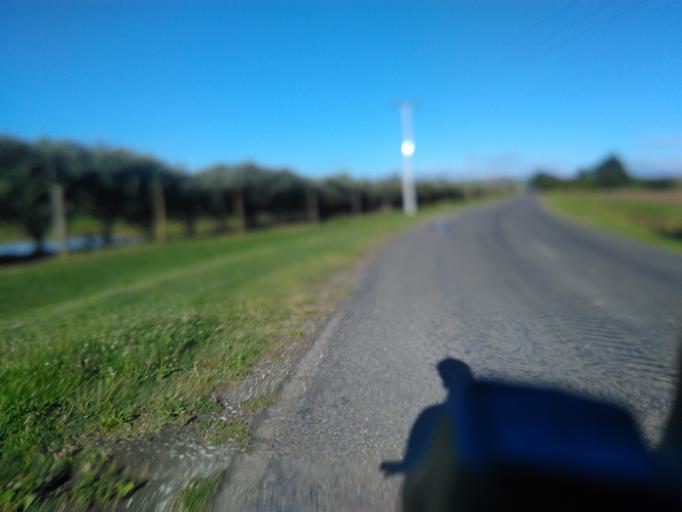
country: NZ
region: Gisborne
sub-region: Gisborne District
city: Gisborne
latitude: -38.5994
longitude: 177.9319
